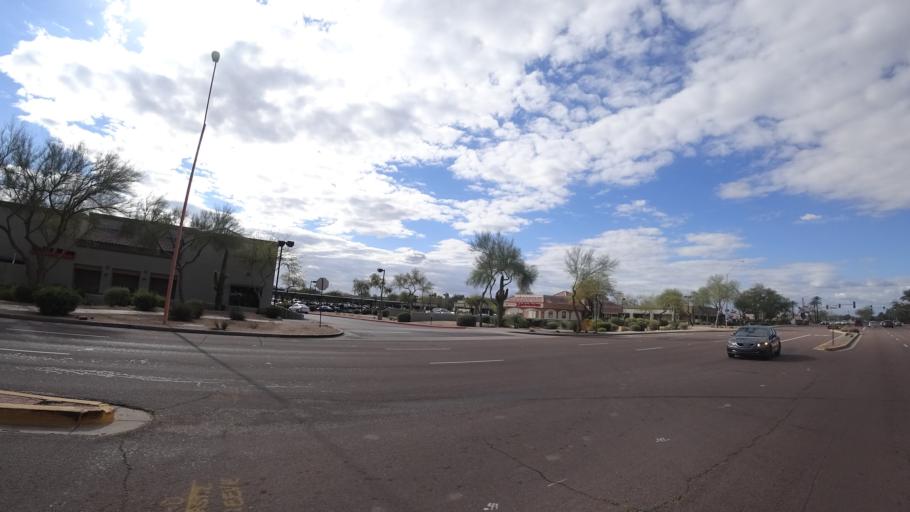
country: US
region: Arizona
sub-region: Maricopa County
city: Paradise Valley
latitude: 33.6205
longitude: -111.8742
